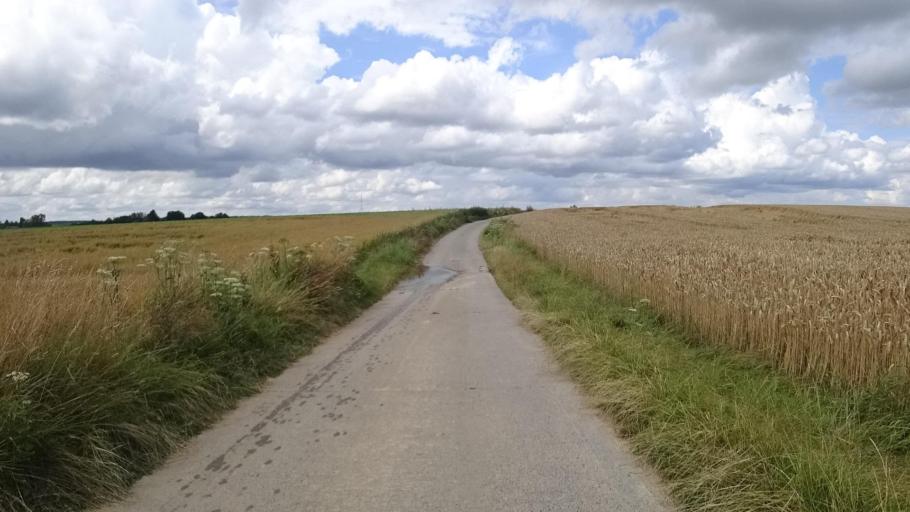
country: BE
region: Wallonia
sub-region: Province du Brabant Wallon
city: Chastre
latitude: 50.5853
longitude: 4.6188
